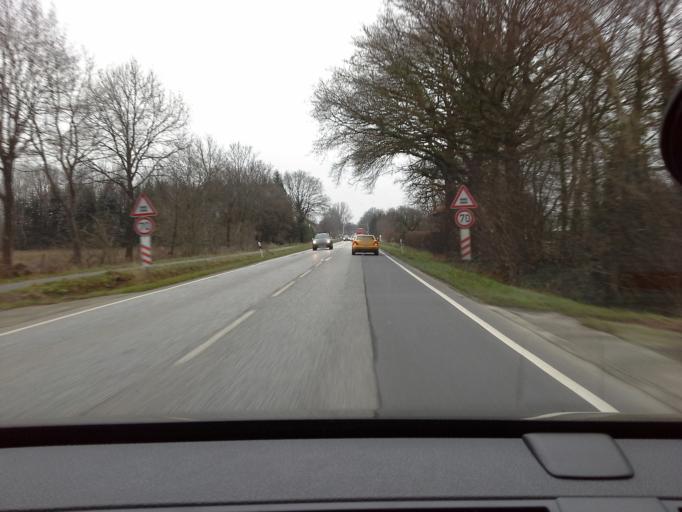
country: DE
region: Schleswig-Holstein
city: Bilsen
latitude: 53.7894
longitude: 9.8758
